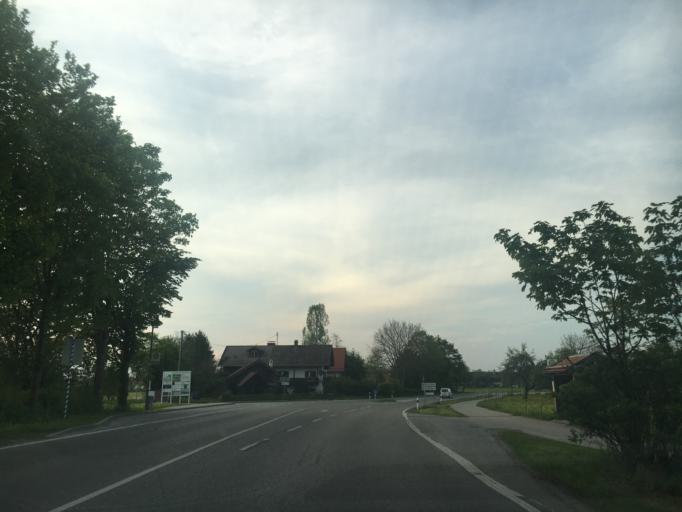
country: DE
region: Bavaria
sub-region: Upper Bavaria
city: Benediktbeuern
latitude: 47.6985
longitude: 11.4050
